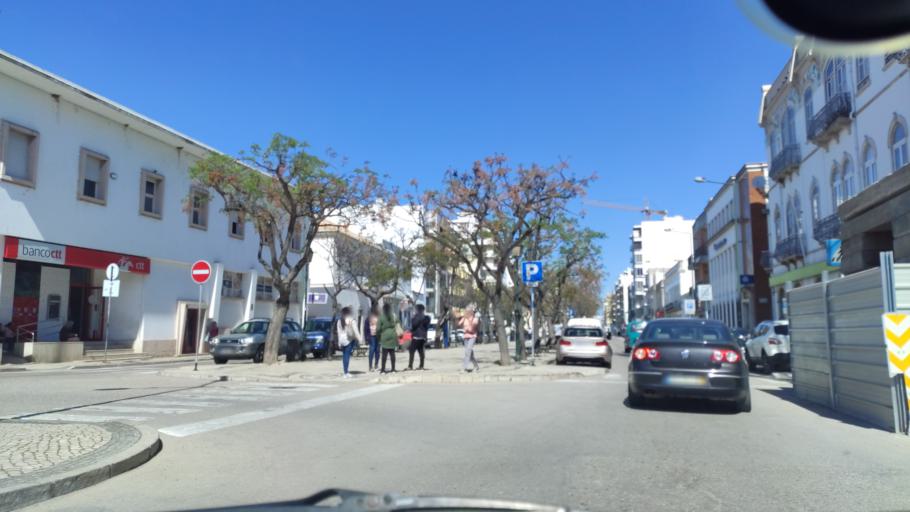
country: PT
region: Faro
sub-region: Olhao
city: Olhao
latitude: 37.0273
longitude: -7.8398
